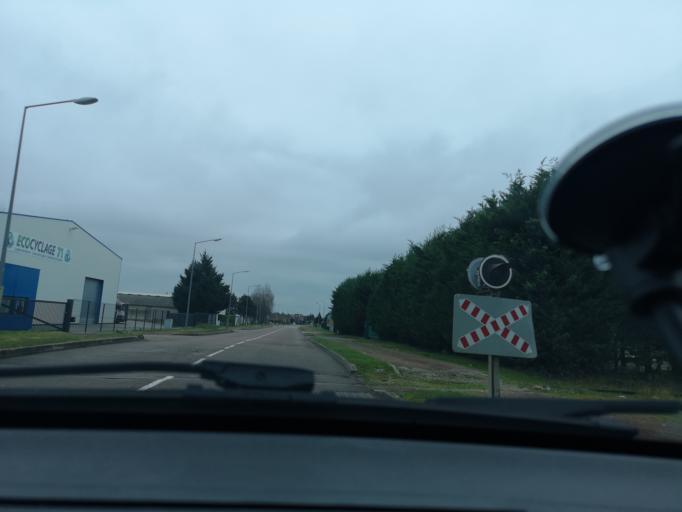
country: FR
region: Bourgogne
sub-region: Departement de Saone-et-Loire
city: Virey-le-Grand
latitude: 46.8235
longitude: 4.8662
